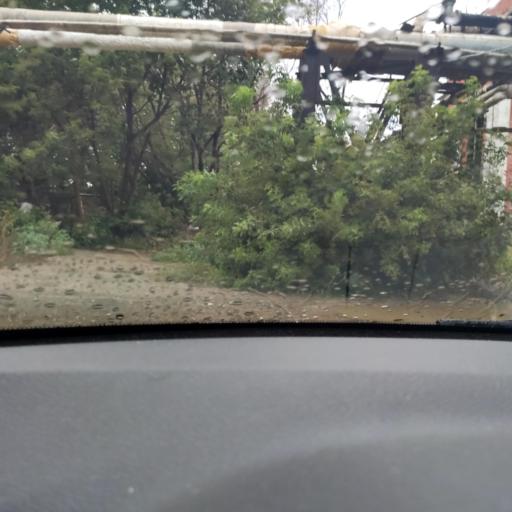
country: RU
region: Samara
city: Samara
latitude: 53.2225
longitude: 50.1473
